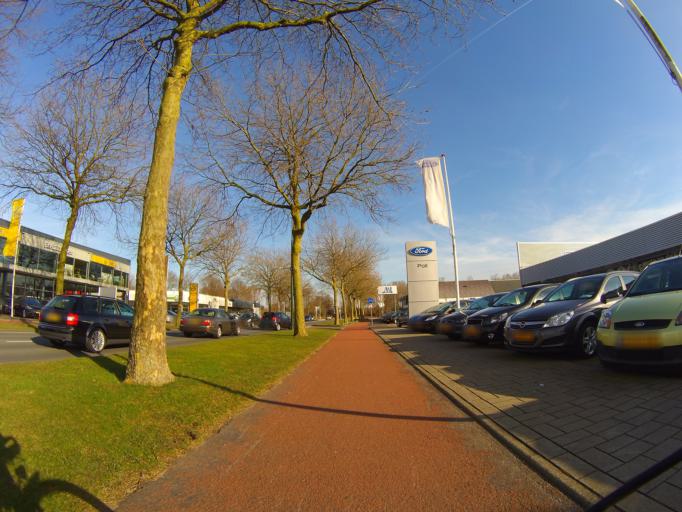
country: NL
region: North Holland
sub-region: Gemeente Huizen
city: Huizen
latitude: 52.3049
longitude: 5.2453
